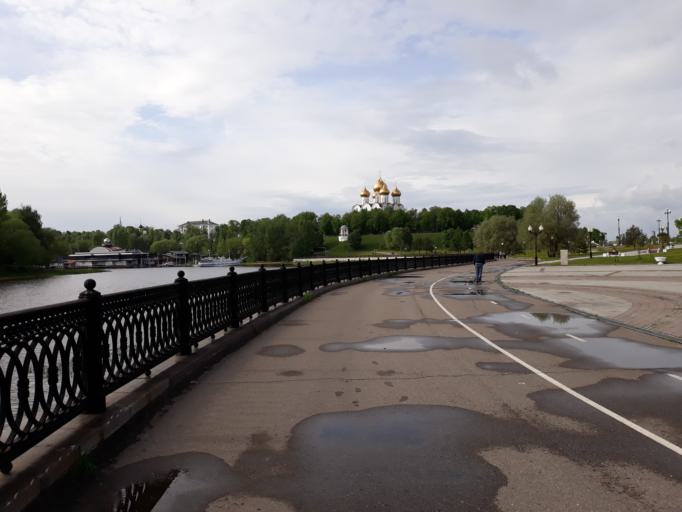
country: RU
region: Jaroslavl
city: Yaroslavl
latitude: 57.6182
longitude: 39.9032
